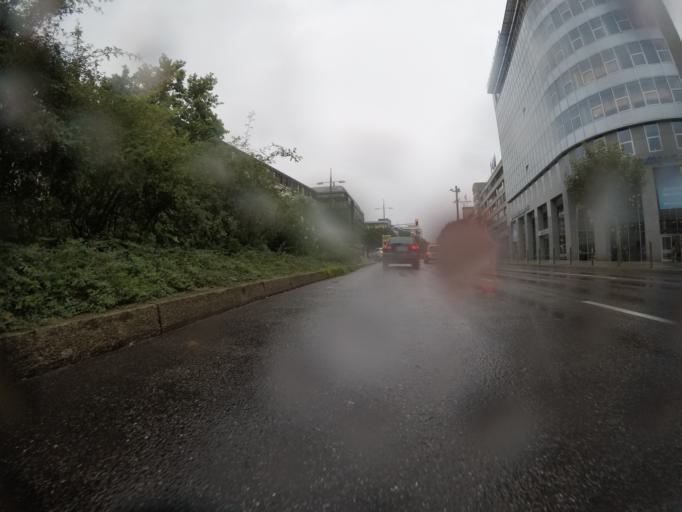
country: DE
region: Baden-Wuerttemberg
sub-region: Regierungsbezirk Stuttgart
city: Stuttgart
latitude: 48.7799
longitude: 9.1766
